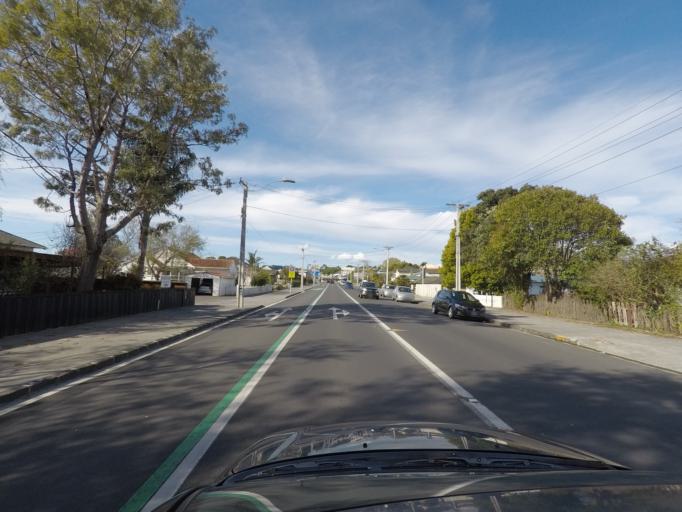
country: NZ
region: Auckland
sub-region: Auckland
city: Rosebank
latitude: -36.9003
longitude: 174.6948
